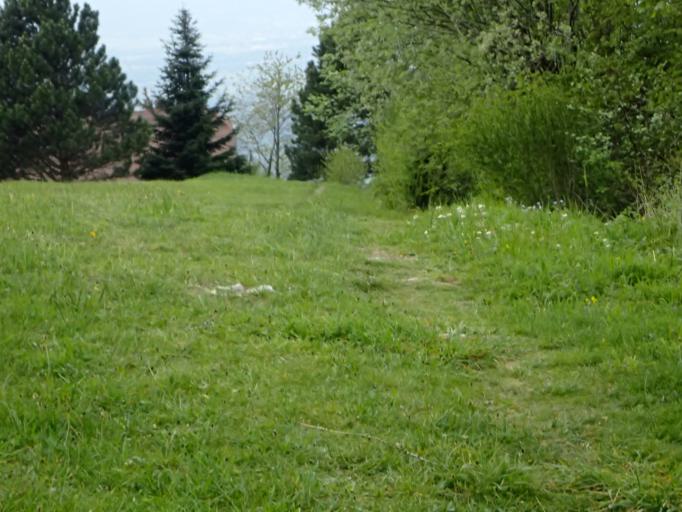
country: AT
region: Salzburg
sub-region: Politischer Bezirk Salzburg-Umgebung
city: Elsbethen
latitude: 47.7529
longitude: 13.1073
